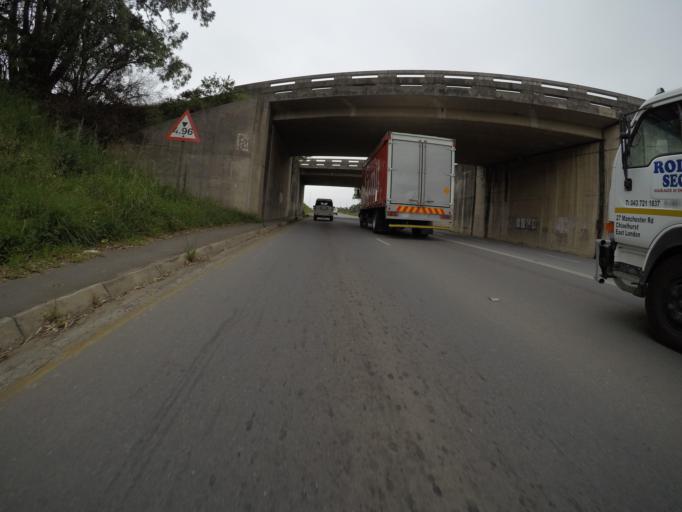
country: ZA
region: Eastern Cape
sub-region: Buffalo City Metropolitan Municipality
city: East London
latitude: -32.9380
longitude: 27.9515
